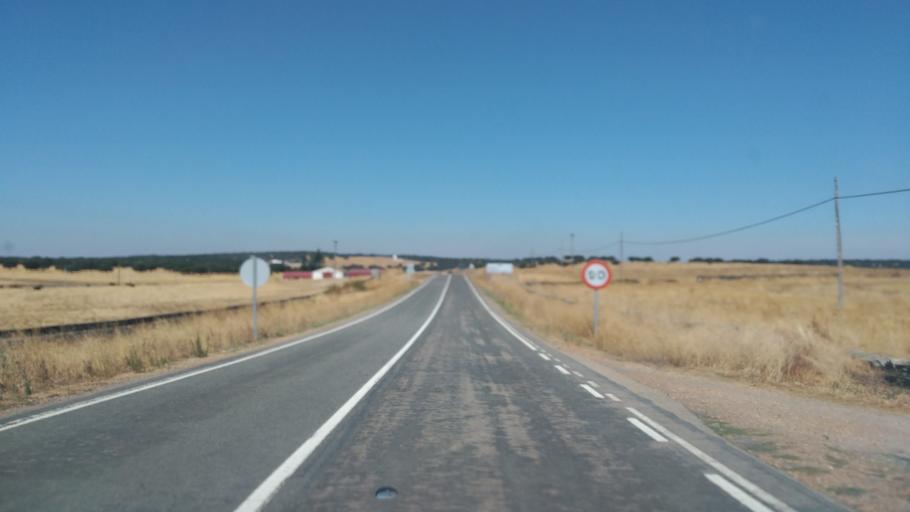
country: ES
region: Castille and Leon
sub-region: Provincia de Salamanca
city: Vecinos
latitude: 40.7787
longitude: -5.8814
